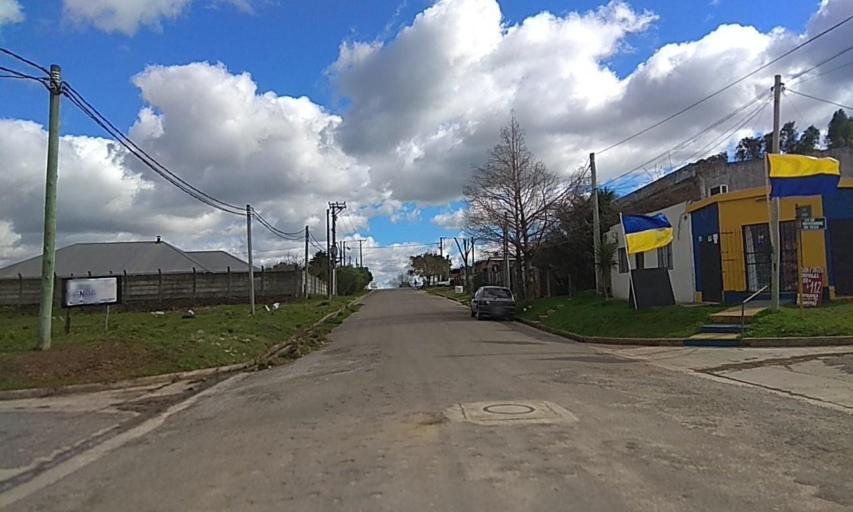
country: UY
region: Florida
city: Florida
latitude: -34.0882
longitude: -56.2314
